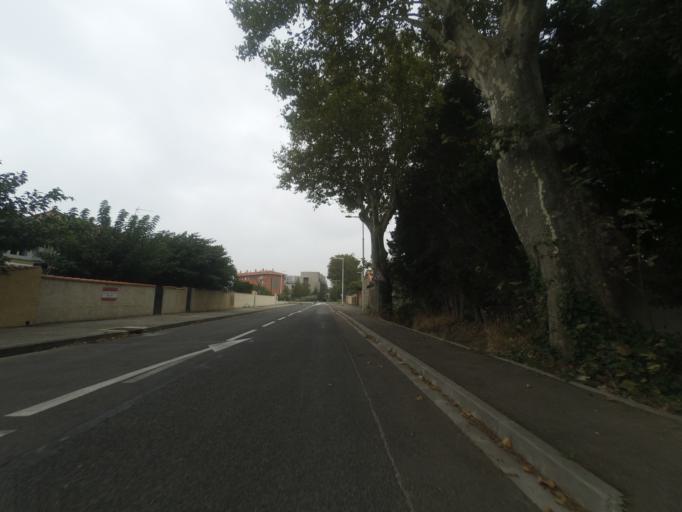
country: FR
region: Languedoc-Roussillon
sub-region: Departement des Pyrenees-Orientales
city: Perpignan
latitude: 42.7033
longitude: 2.8771
